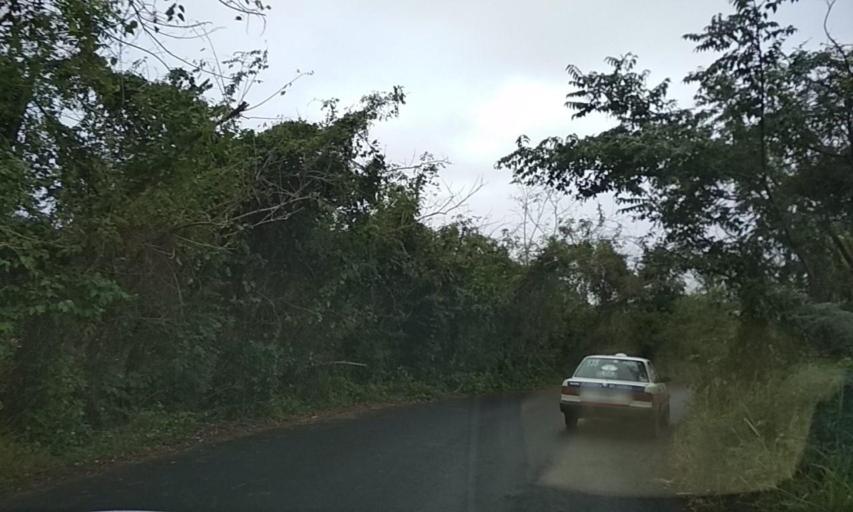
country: MX
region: Veracruz
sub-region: Coatzintla
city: Manuel Maria Contreras
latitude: 20.4456
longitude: -97.4926
